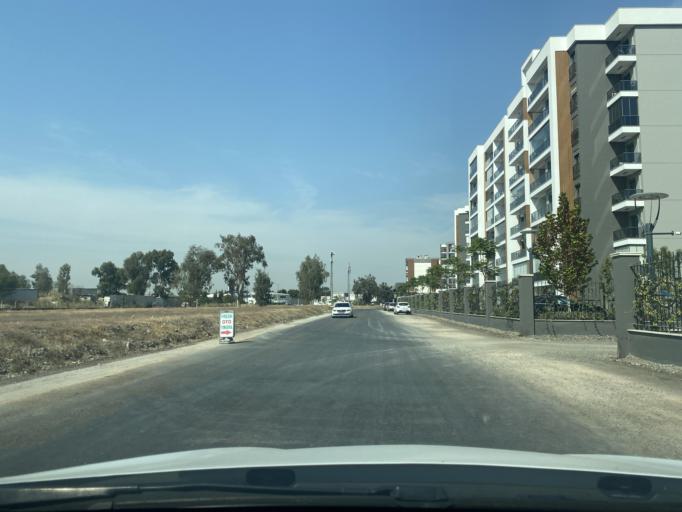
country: TR
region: Izmir
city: Karsiyaka
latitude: 38.4917
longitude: 27.0483
